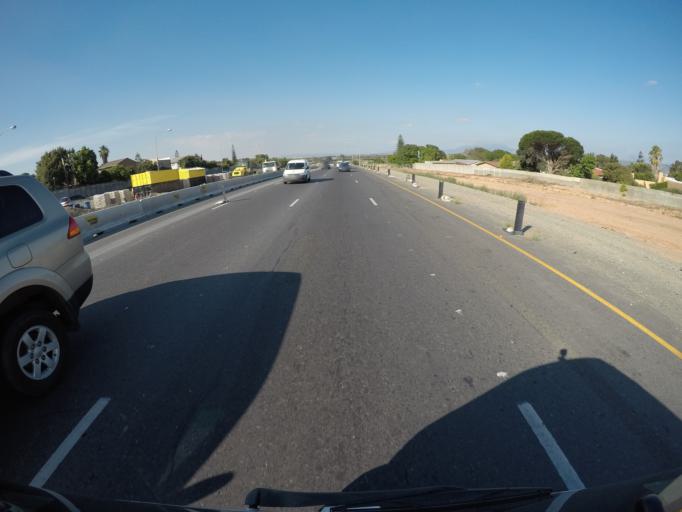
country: ZA
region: Western Cape
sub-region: City of Cape Town
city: Kraaifontein
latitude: -33.8761
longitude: 18.6612
